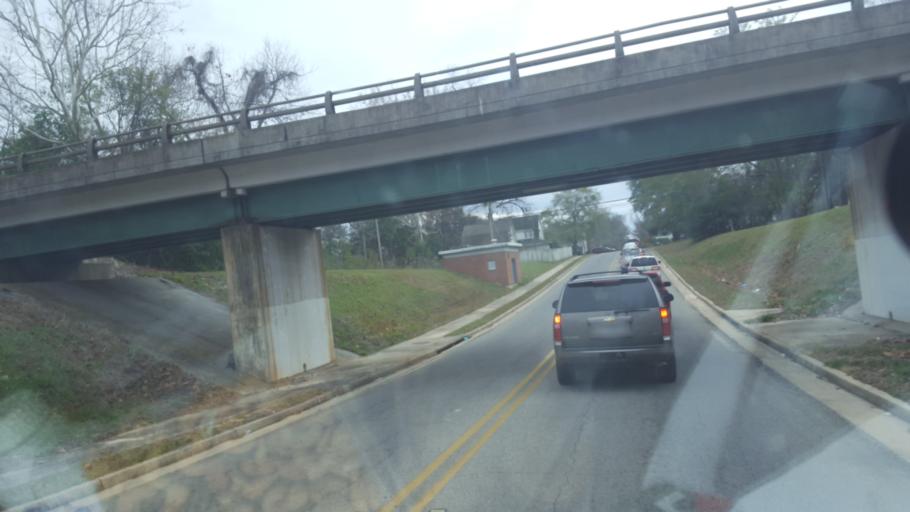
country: US
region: Georgia
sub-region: Ben Hill County
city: Fitzgerald
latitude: 31.7162
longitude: -83.2599
